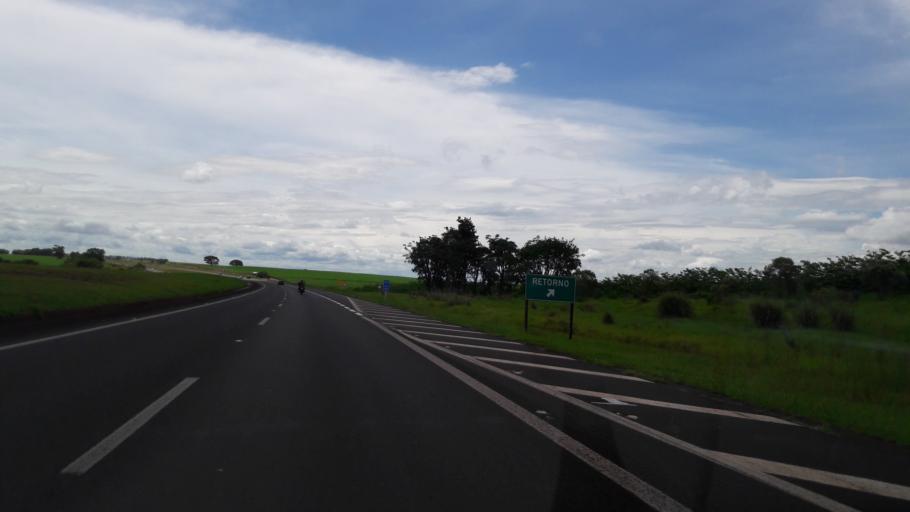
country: BR
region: Sao Paulo
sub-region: Avare
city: Avare
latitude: -22.9416
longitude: -48.9060
